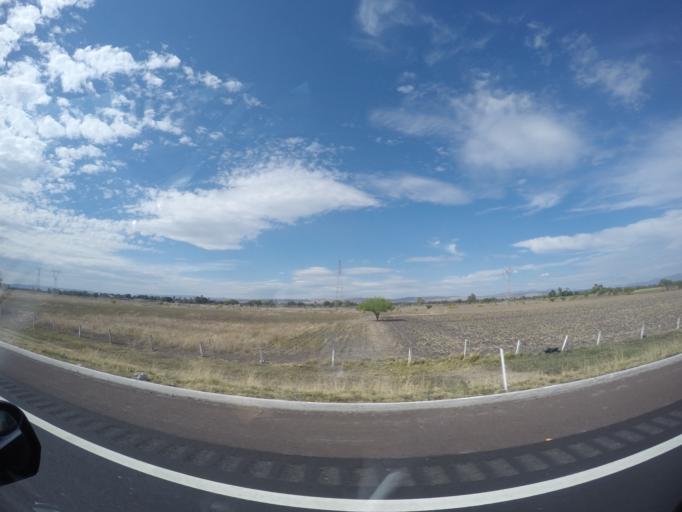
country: MX
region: Guanajuato
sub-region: Celaya
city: Colonia Patria Nueva
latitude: 20.5705
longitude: -100.8931
